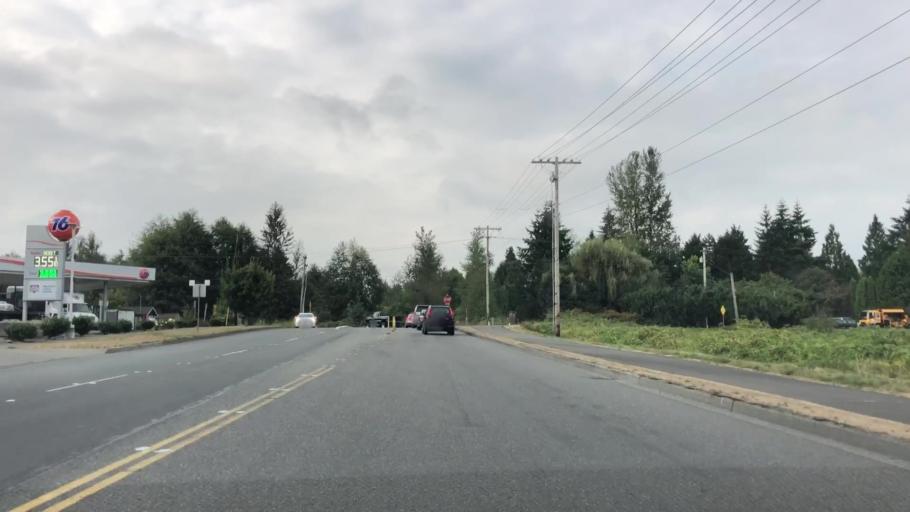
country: US
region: Washington
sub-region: Snohomish County
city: Monroe
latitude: 47.8497
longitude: -122.0121
